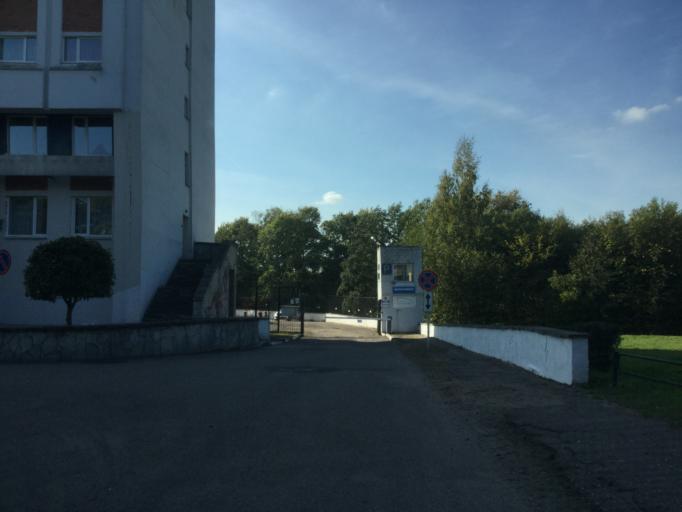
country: BY
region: Vitebsk
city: Vitebsk
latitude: 55.1748
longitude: 30.1955
